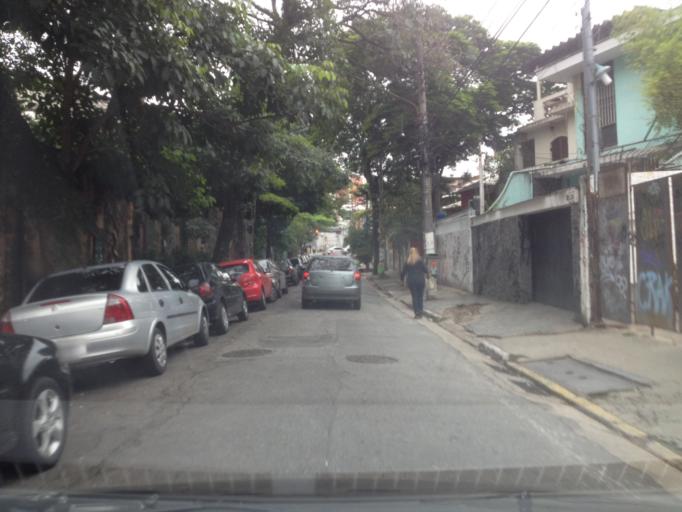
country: BR
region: Sao Paulo
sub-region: Sao Paulo
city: Sao Paulo
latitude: -23.5599
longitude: -46.6872
